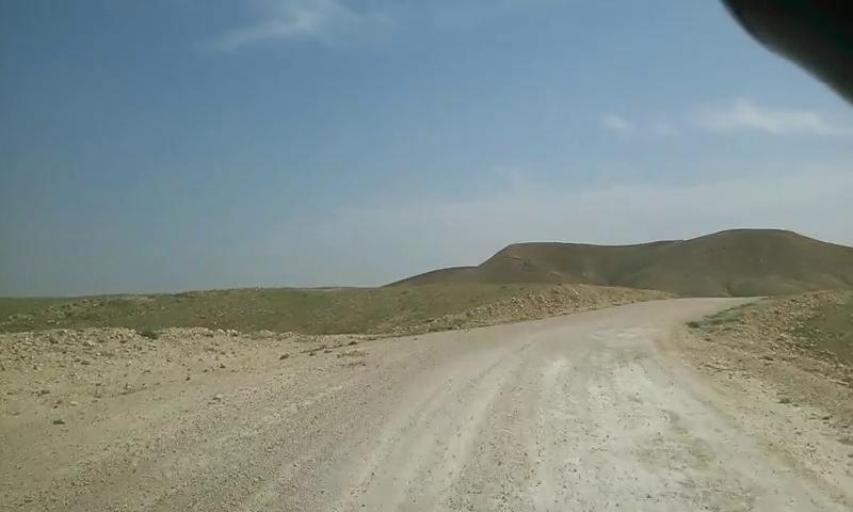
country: PS
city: `Arab ar Rashaydah
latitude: 31.4992
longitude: 35.2942
